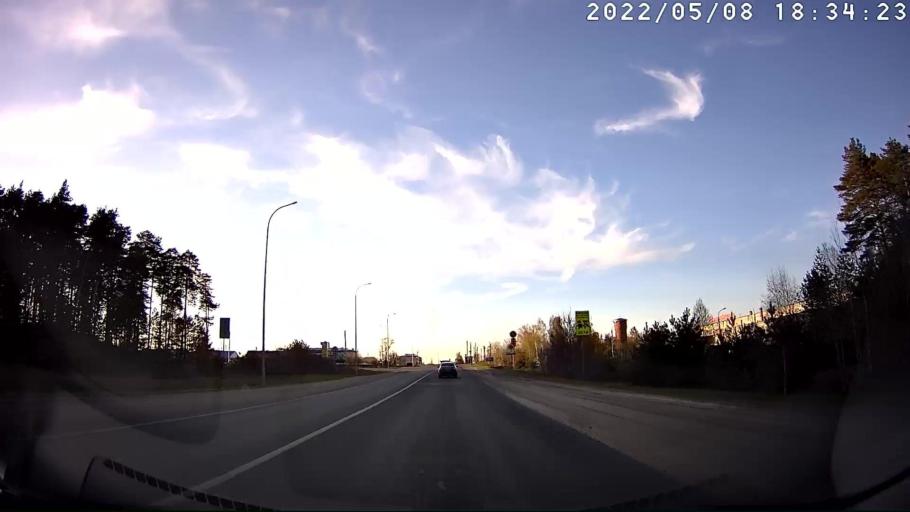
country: RU
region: Mariy-El
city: Volzhsk
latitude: 55.8998
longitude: 48.3563
